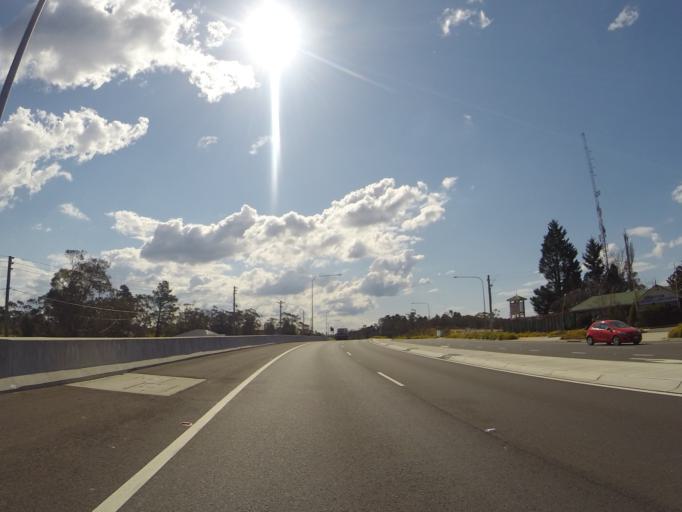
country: AU
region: New South Wales
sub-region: Blue Mountains Municipality
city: Lawson
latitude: -33.7244
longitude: 150.3845
